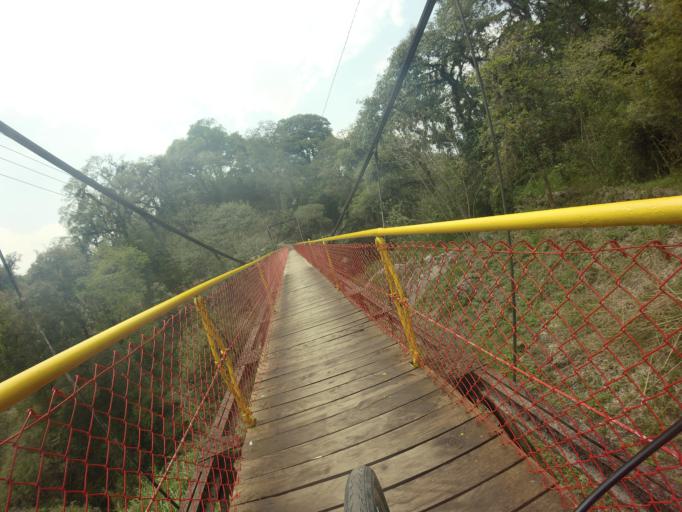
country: MX
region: Veracruz
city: Xico
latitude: 19.4022
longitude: -96.9942
